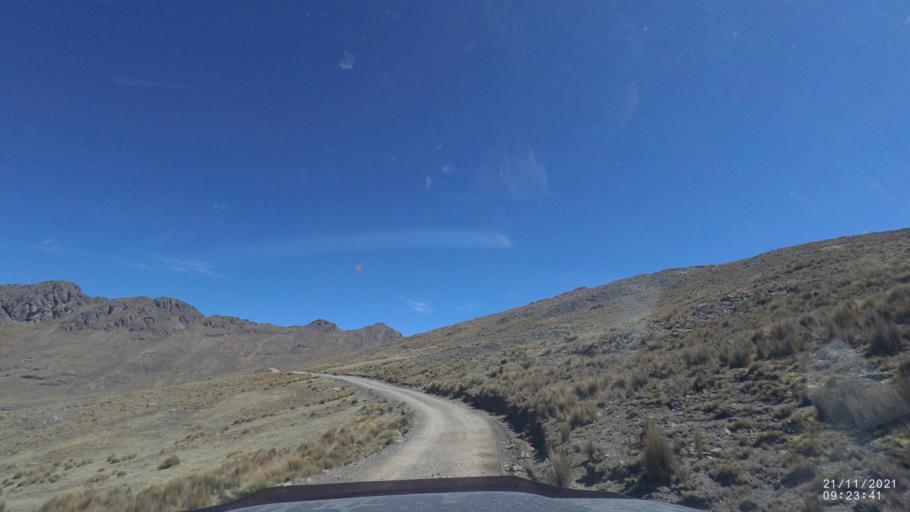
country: BO
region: Cochabamba
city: Cochabamba
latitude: -17.0962
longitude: -66.2536
